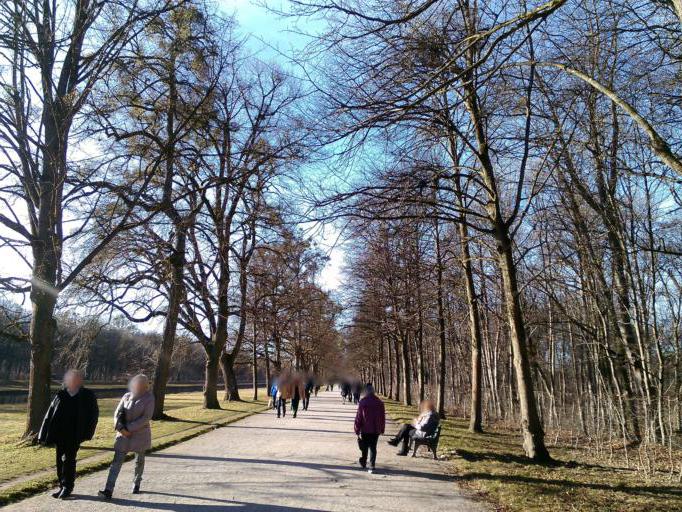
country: DE
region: Bavaria
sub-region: Upper Bavaria
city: Pasing
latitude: 48.1583
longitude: 11.4969
